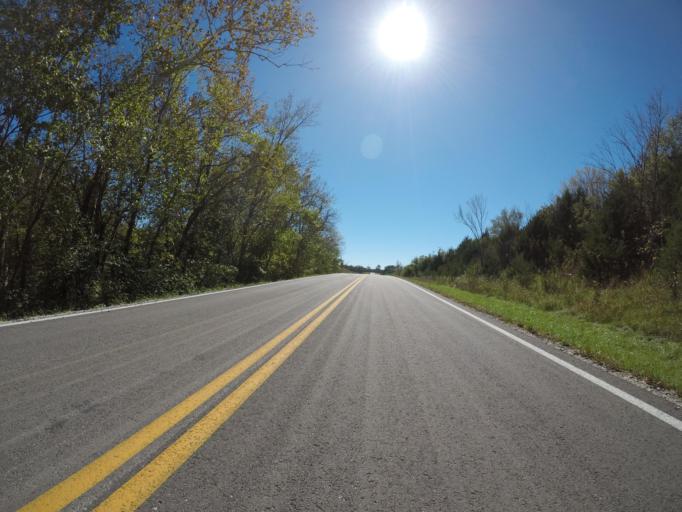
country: US
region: Kansas
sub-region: Johnson County
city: De Soto
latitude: 38.9630
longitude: -95.0195
